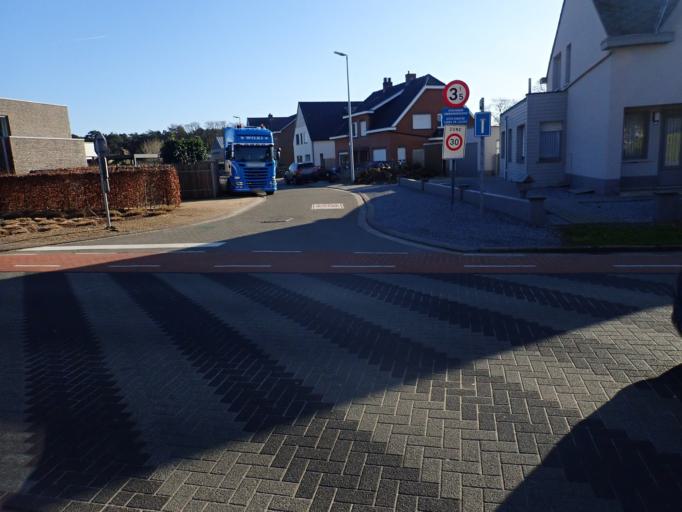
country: BE
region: Flanders
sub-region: Provincie Antwerpen
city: Olen
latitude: 51.1234
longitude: 4.8327
